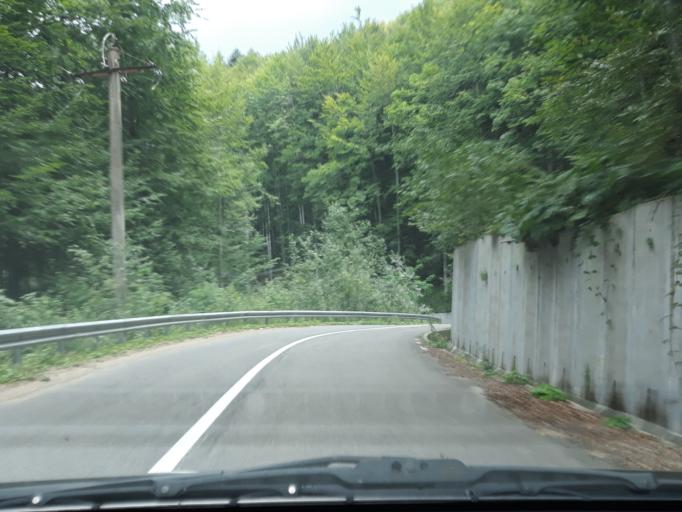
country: RO
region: Bihor
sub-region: Comuna Pietroasa
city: Pietroasa
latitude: 46.5908
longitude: 22.6724
